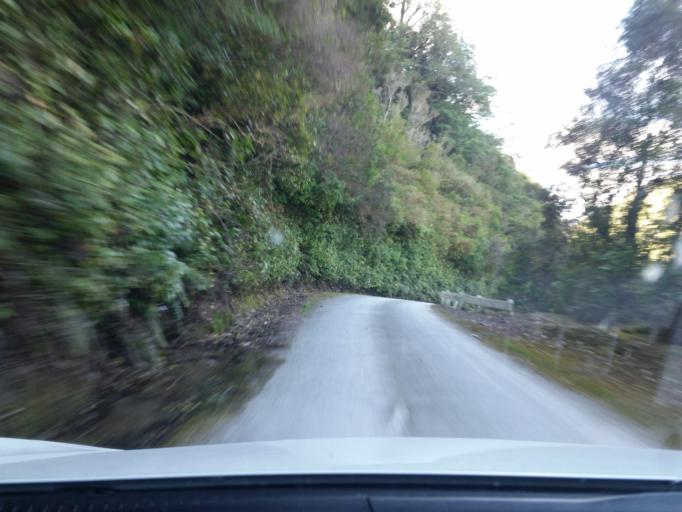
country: NZ
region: West Coast
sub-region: Buller District
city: Westport
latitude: -41.7755
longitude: 172.2201
